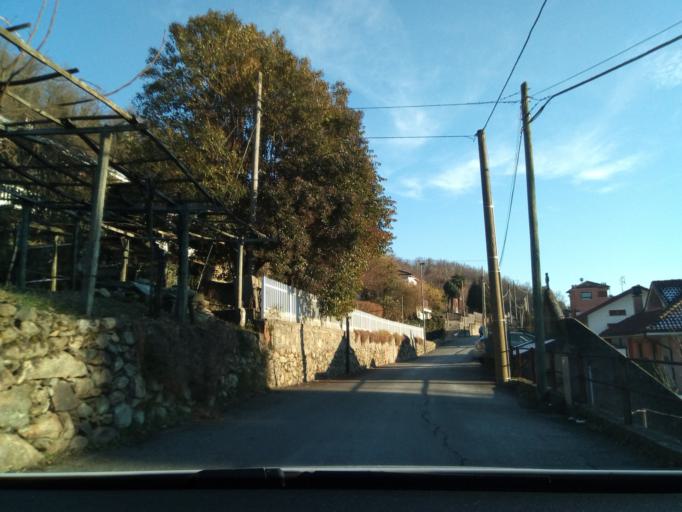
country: IT
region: Piedmont
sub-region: Provincia di Torino
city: Burolo
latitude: 45.4814
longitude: 7.9353
